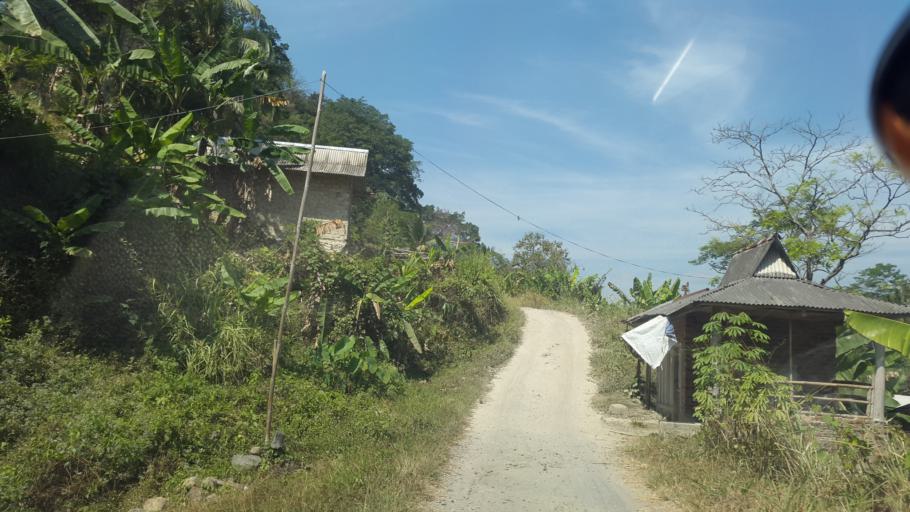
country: ID
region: West Java
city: Bojonggaling
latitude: -6.9321
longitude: 106.6091
